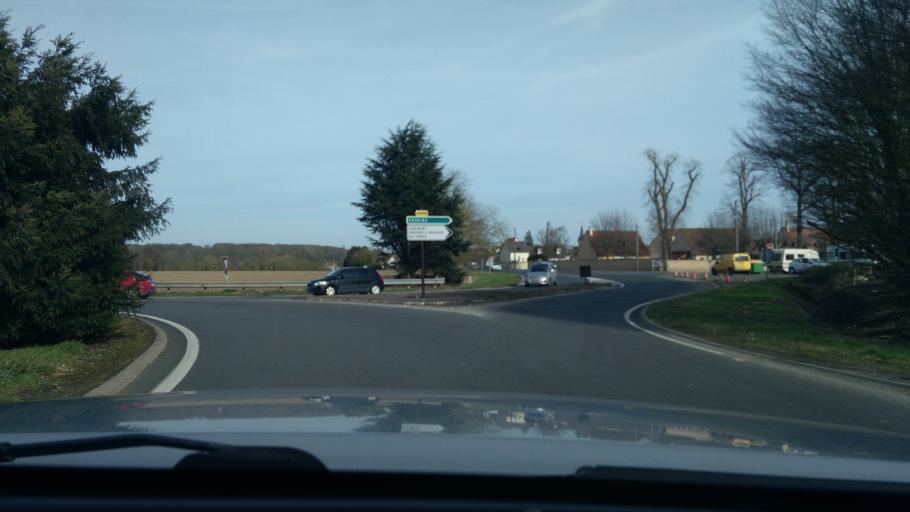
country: FR
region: Ile-de-France
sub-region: Departement de Seine-et-Marne
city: Guignes
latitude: 48.6356
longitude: 2.7880
